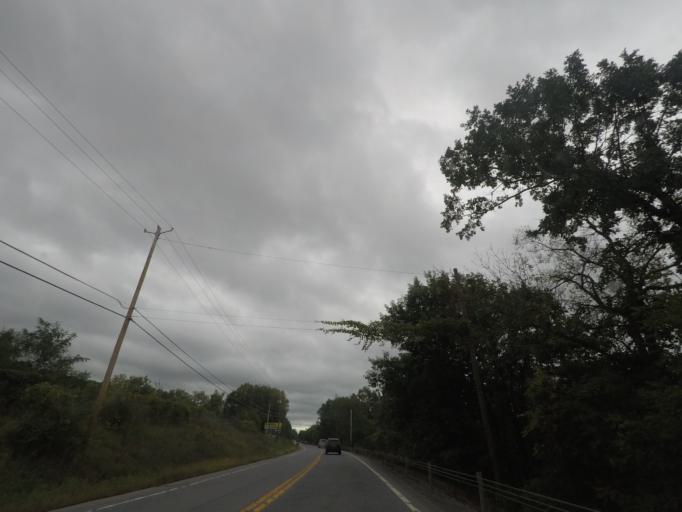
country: US
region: New York
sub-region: Saratoga County
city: Mechanicville
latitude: 42.9167
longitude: -73.7104
